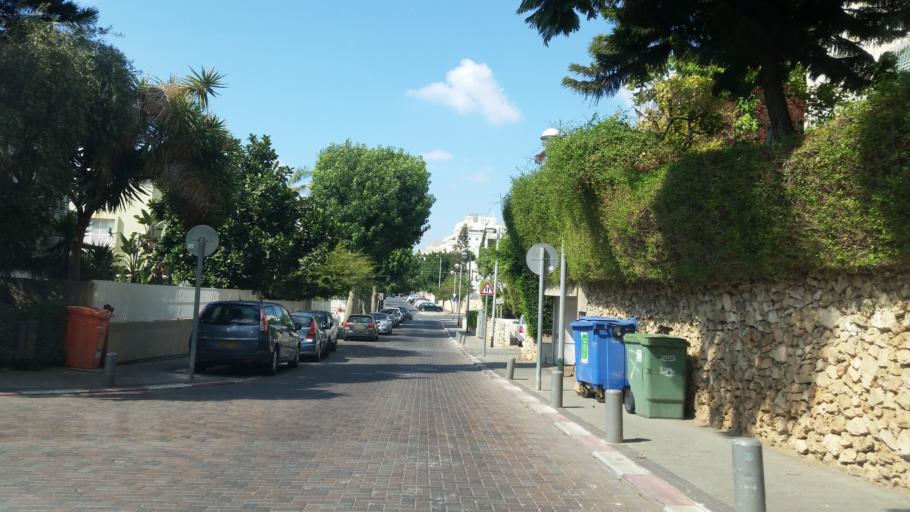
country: IL
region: Tel Aviv
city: Ramat HaSharon
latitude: 32.1151
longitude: 34.8271
